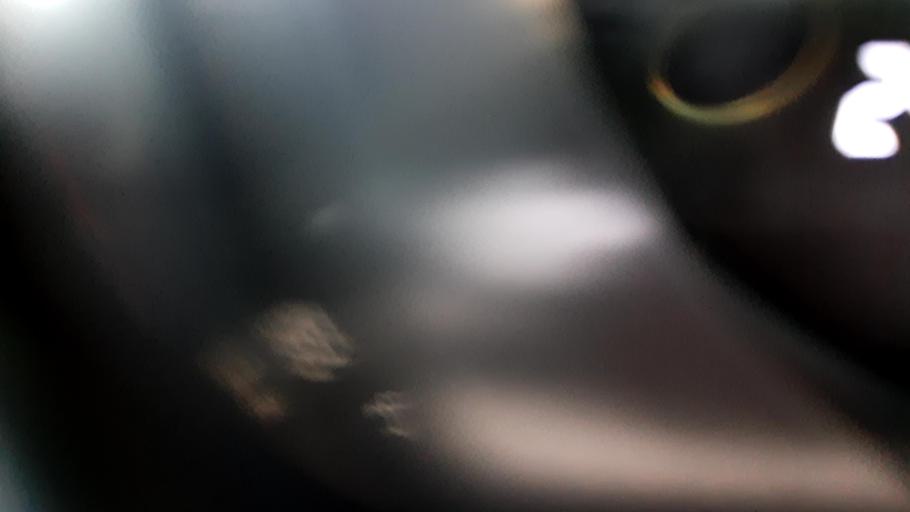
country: RU
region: Nizjnij Novgorod
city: Bor
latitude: 56.3640
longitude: 44.0727
